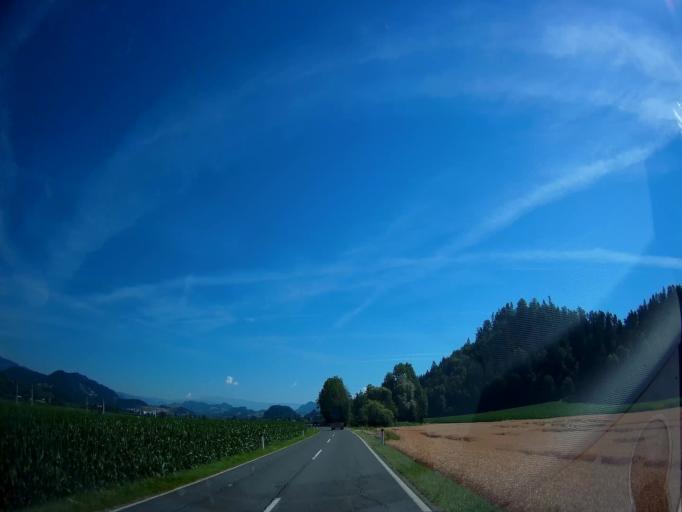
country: AT
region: Carinthia
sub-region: Politischer Bezirk Klagenfurt Land
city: Maria Saal
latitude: 46.7085
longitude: 14.3667
